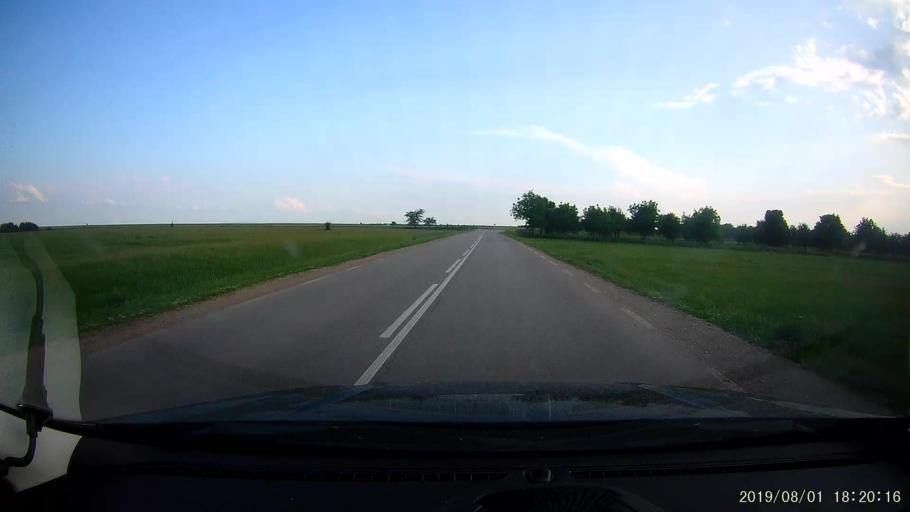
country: BG
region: Shumen
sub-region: Obshtina Kaolinovo
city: Kaolinovo
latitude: 43.6744
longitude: 27.0898
